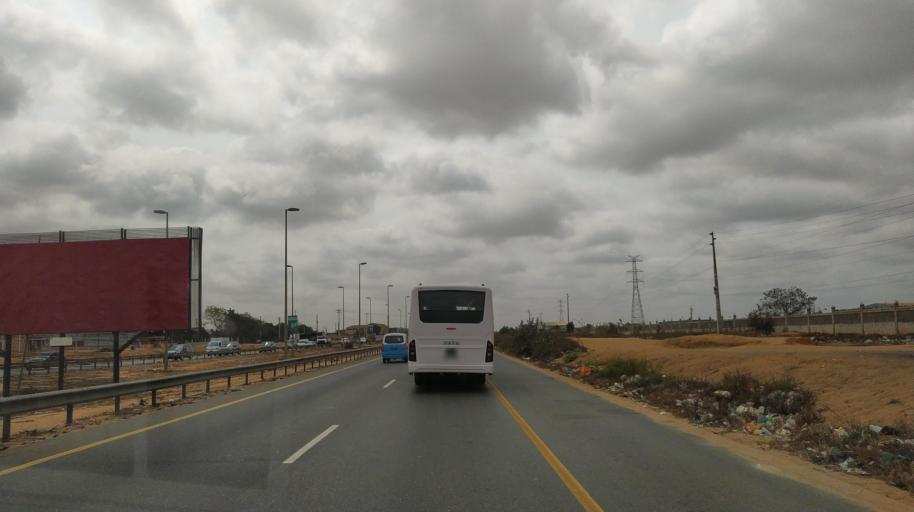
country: AO
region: Luanda
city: Luanda
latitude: -8.9732
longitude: 13.3320
